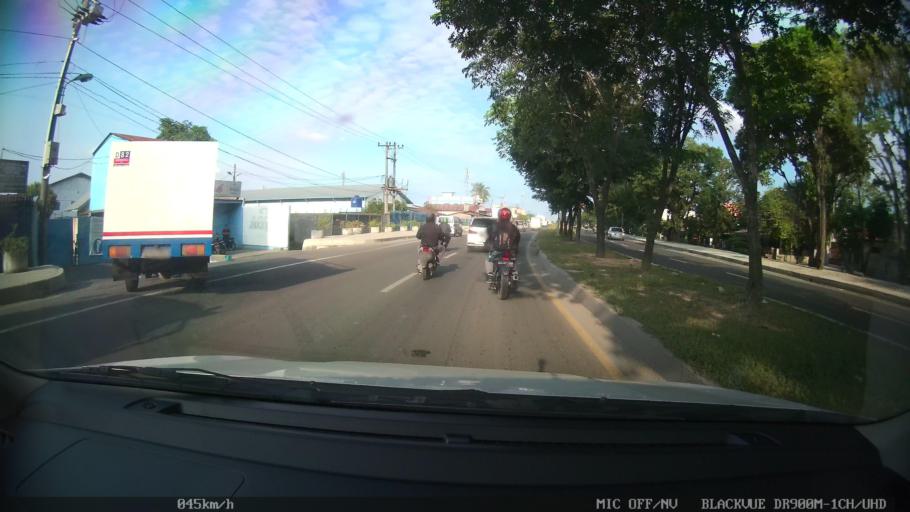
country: ID
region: North Sumatra
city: Sunggal
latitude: 3.6159
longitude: 98.6301
